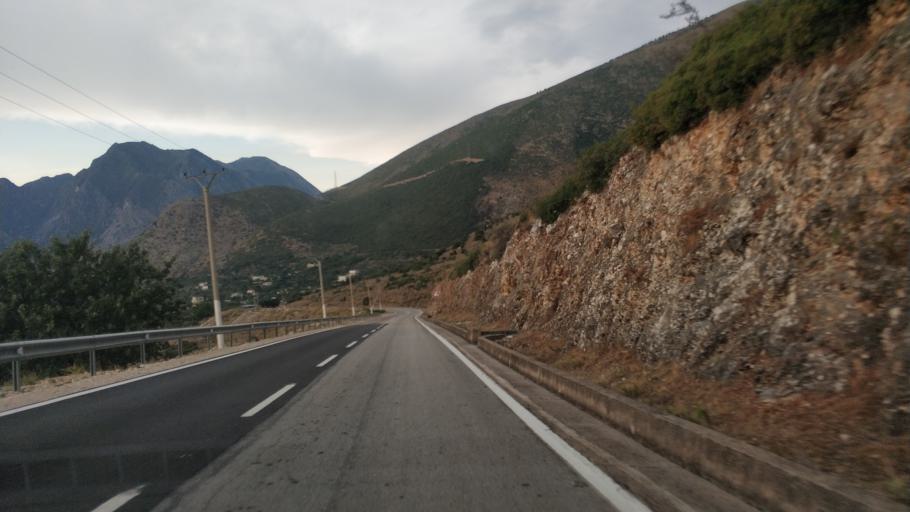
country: AL
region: Vlore
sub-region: Rrethi i Sarandes
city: Lukove
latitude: 40.0446
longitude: 19.8714
